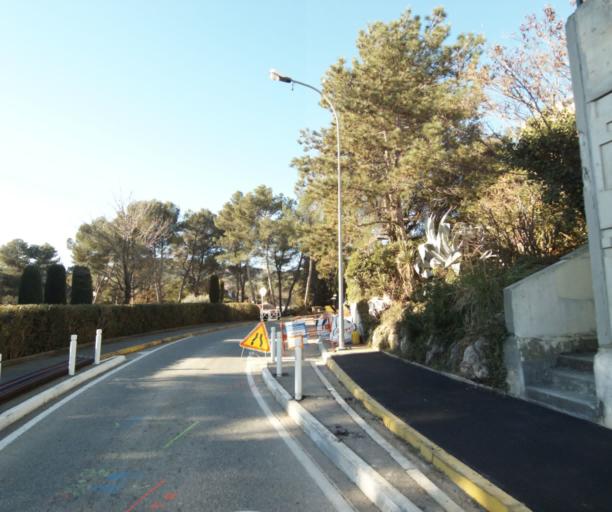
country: FR
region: Provence-Alpes-Cote d'Azur
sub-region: Departement des Alpes-Maritimes
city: Vallauris
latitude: 43.5962
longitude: 7.0690
